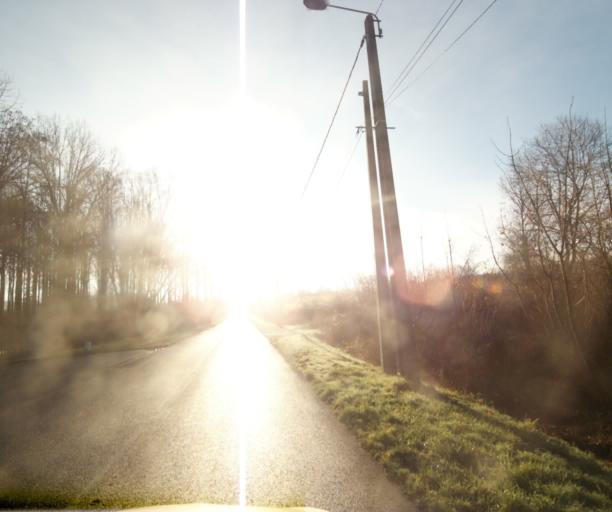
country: FR
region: Nord-Pas-de-Calais
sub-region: Departement du Nord
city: Vicq
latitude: 50.4017
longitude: 3.5825
